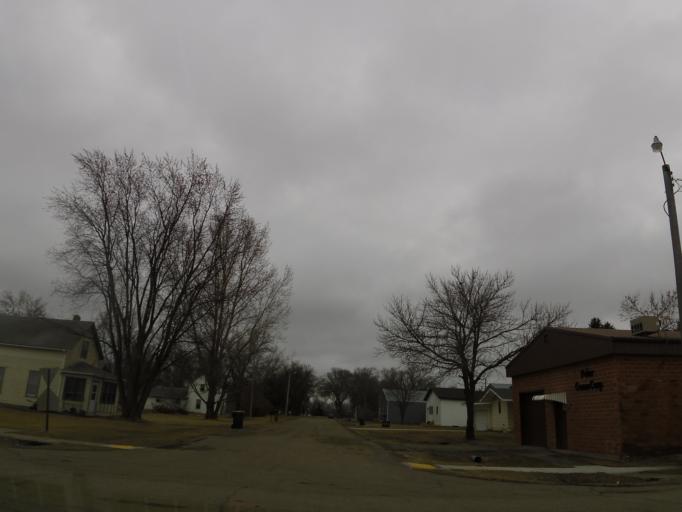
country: US
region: North Dakota
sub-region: Traill County
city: Hillsboro
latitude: 47.1907
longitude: -97.2161
